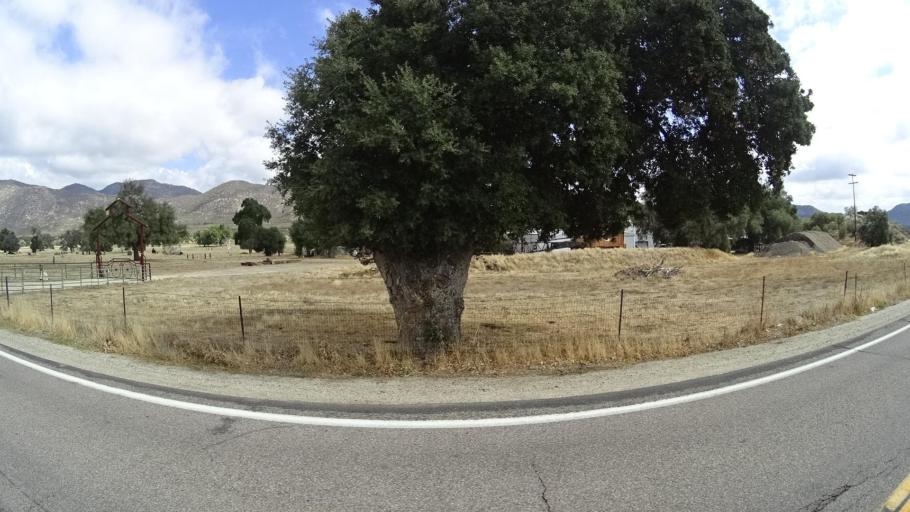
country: US
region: California
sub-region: San Diego County
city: Pine Valley
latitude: 32.7490
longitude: -116.4939
